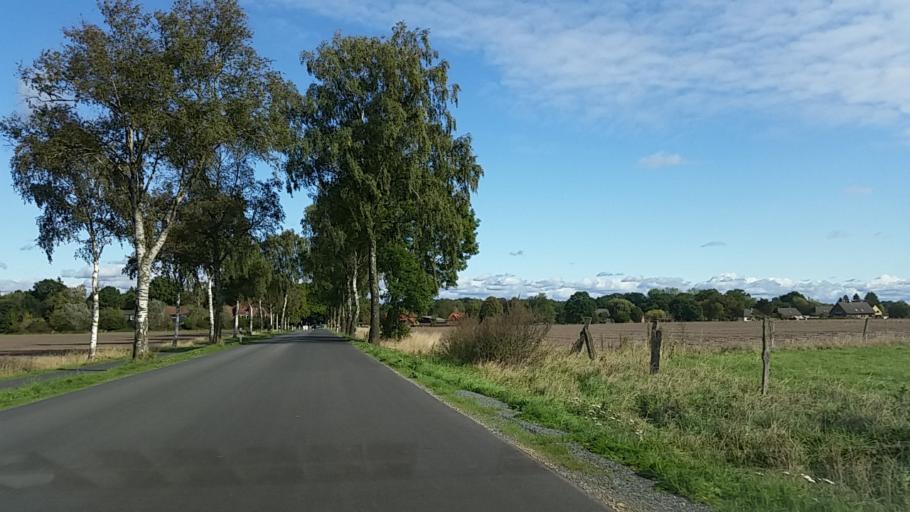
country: DE
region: Lower Saxony
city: Visselhovede
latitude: 53.0048
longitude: 9.6113
